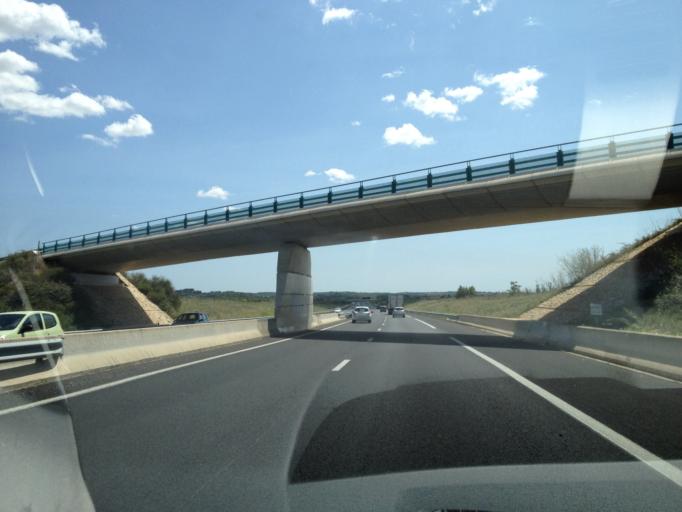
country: FR
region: Languedoc-Roussillon
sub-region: Departement de l'Herault
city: Lezignan-la-Cebe
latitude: 43.5077
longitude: 3.4434
